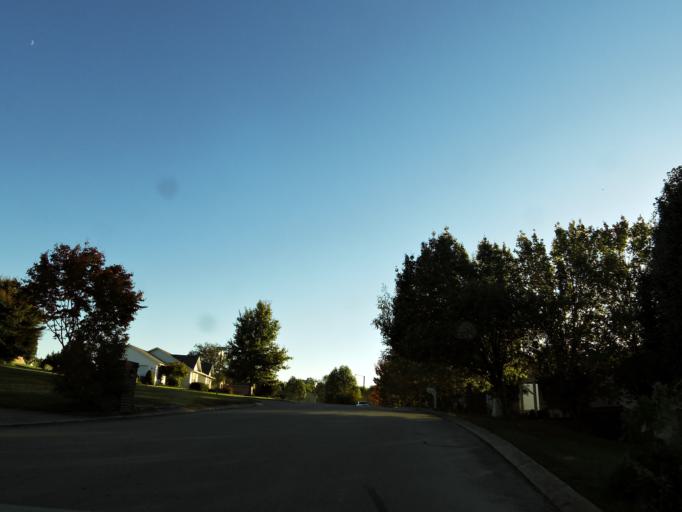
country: US
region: Tennessee
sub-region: Blount County
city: Eagleton Village
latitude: 35.7741
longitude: -83.9183
